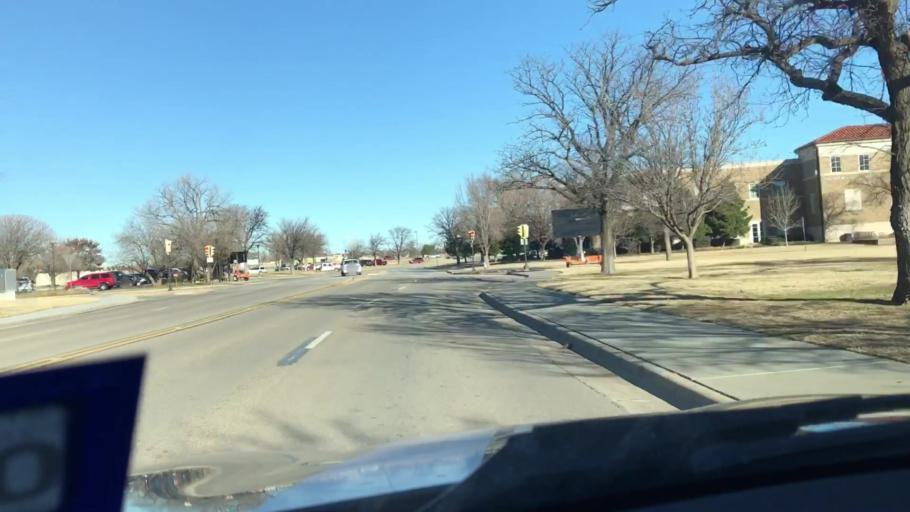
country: US
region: Texas
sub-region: Lubbock County
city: Lubbock
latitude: 33.5850
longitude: -101.8820
